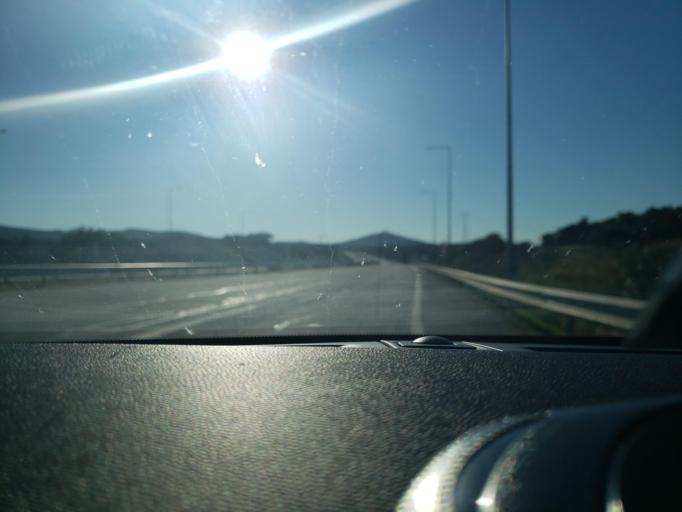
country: PT
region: Evora
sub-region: Estremoz
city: Estremoz
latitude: 38.8009
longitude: -7.6620
